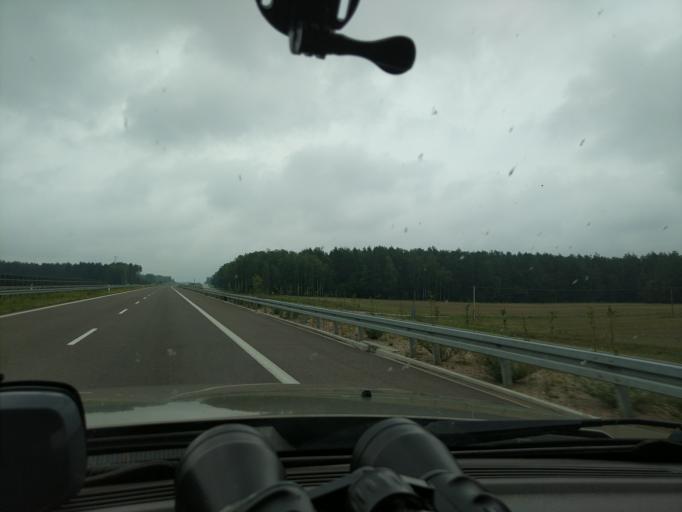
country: PL
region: Podlasie
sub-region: Powiat zambrowski
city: Rutki-Kossaki
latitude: 53.0636
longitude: 22.4085
